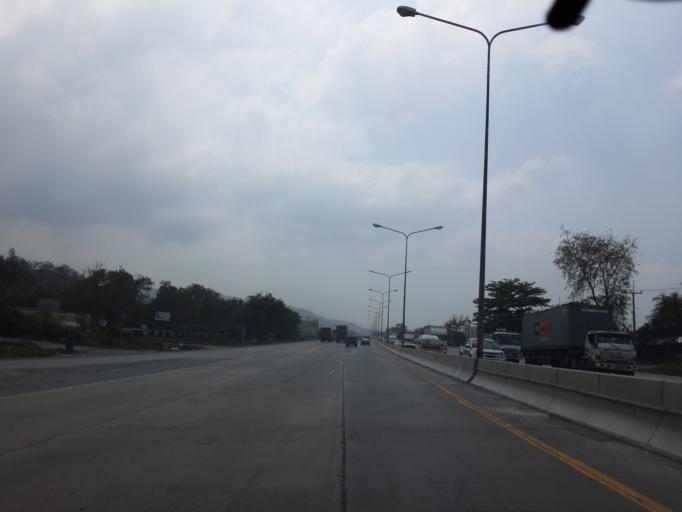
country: TH
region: Chon Buri
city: Chon Buri
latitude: 13.3274
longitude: 100.9900
